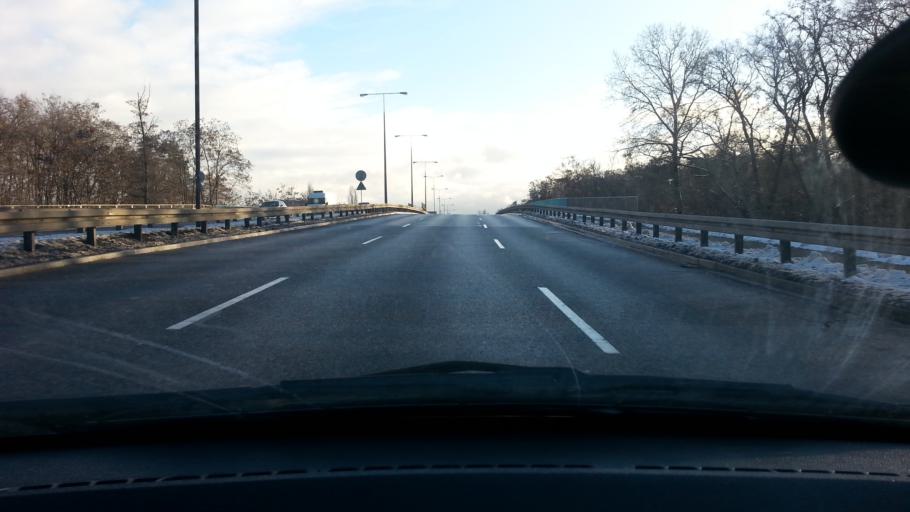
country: PL
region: Masovian Voivodeship
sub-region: Warszawa
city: Zoliborz
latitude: 52.2538
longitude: 20.9540
